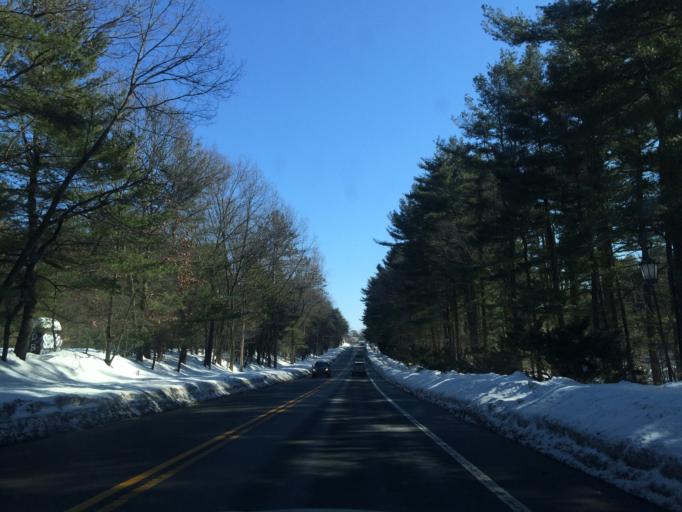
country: US
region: Massachusetts
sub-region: Norfolk County
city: Wellesley
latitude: 42.2962
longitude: -71.3044
